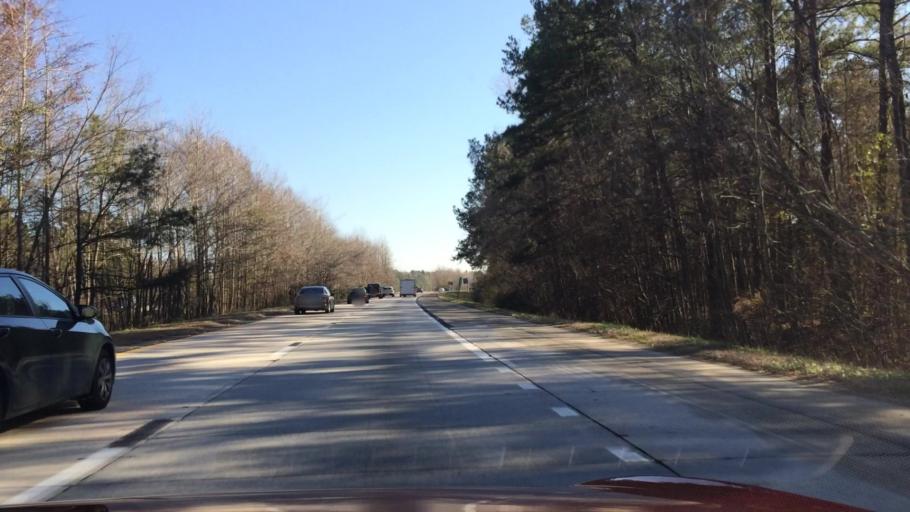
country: US
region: South Carolina
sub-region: Orangeburg County
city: Holly Hill
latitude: 33.2649
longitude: -80.4813
